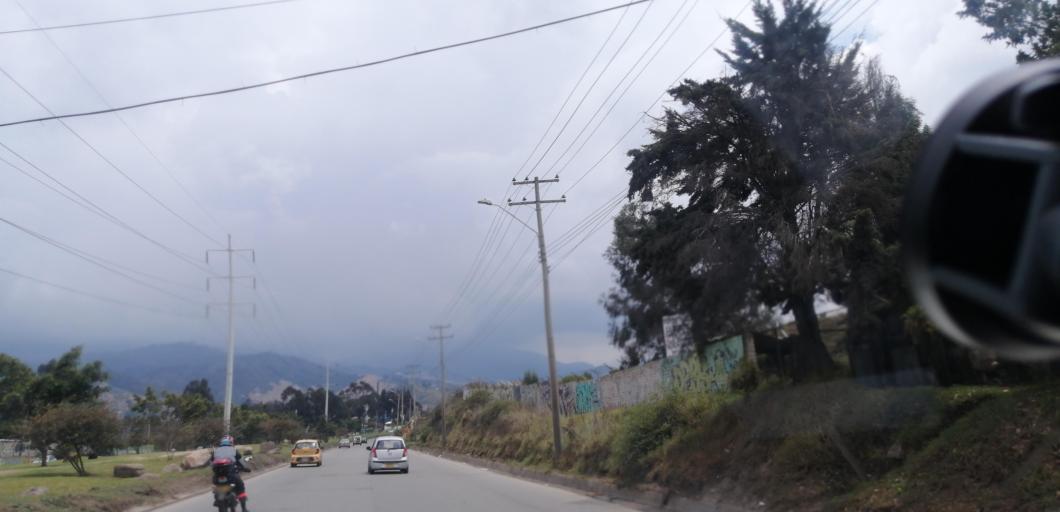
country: CO
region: Bogota D.C.
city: Bogota
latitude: 4.5377
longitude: -74.1309
